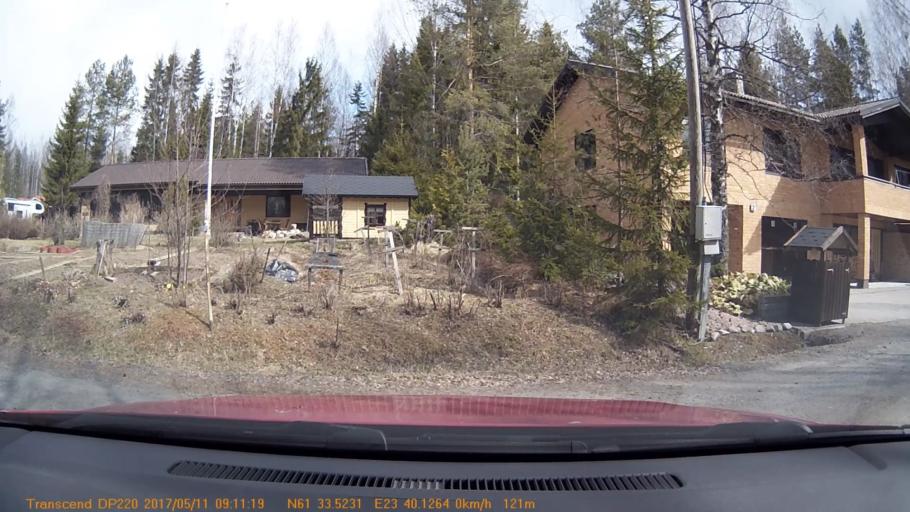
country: FI
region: Pirkanmaa
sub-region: Tampere
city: Yloejaervi
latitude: 61.5587
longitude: 23.6688
